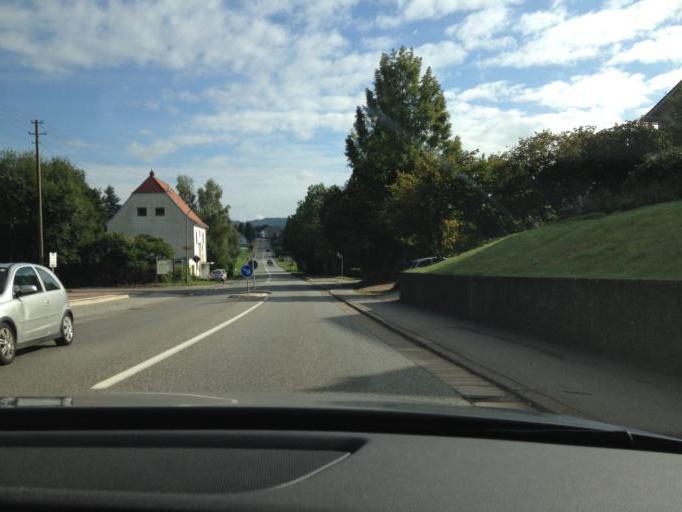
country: DE
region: Saarland
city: Namborn
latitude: 49.5253
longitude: 7.1637
